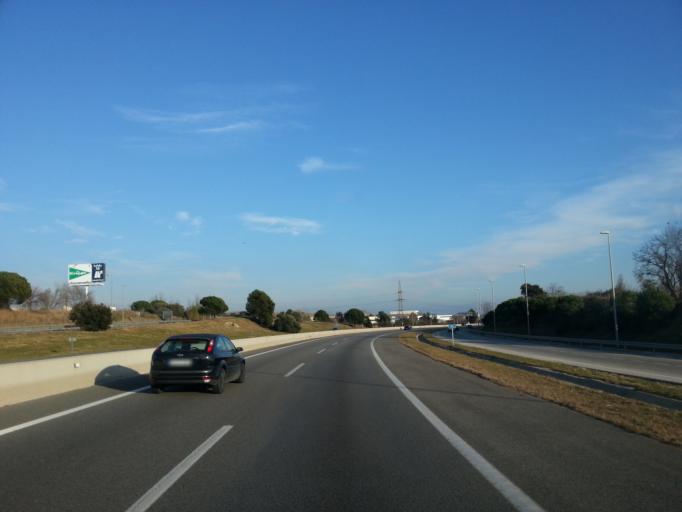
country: ES
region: Catalonia
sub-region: Provincia de Barcelona
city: Terrassa
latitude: 41.5460
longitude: 2.0336
